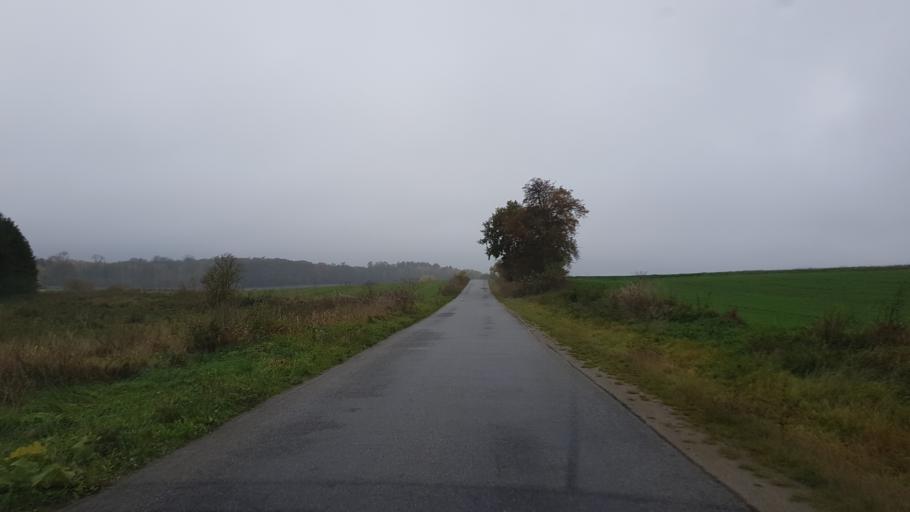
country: PL
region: West Pomeranian Voivodeship
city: Trzcinsko Zdroj
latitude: 53.0571
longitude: 14.5278
